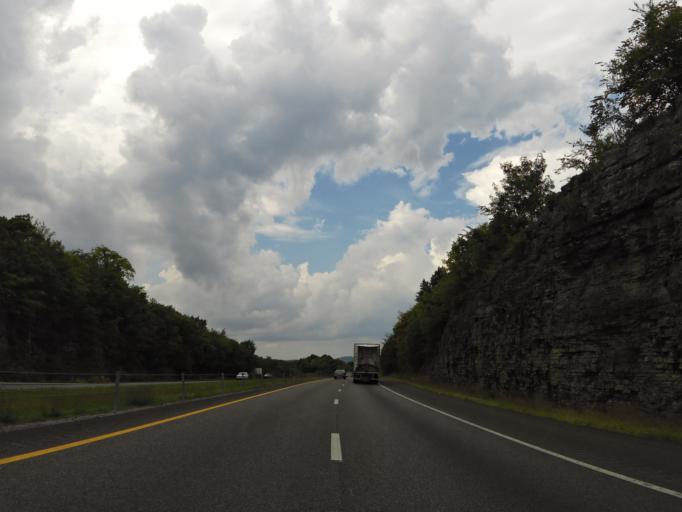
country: US
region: Tennessee
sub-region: Wilson County
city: Watertown
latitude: 36.1701
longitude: -86.0602
